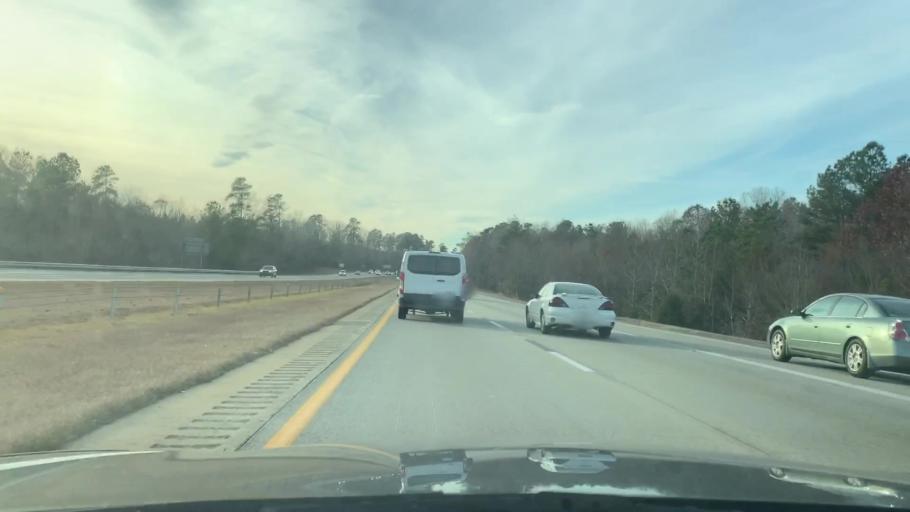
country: US
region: North Carolina
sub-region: Orange County
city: Hillsborough
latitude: 36.0378
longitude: -79.1015
